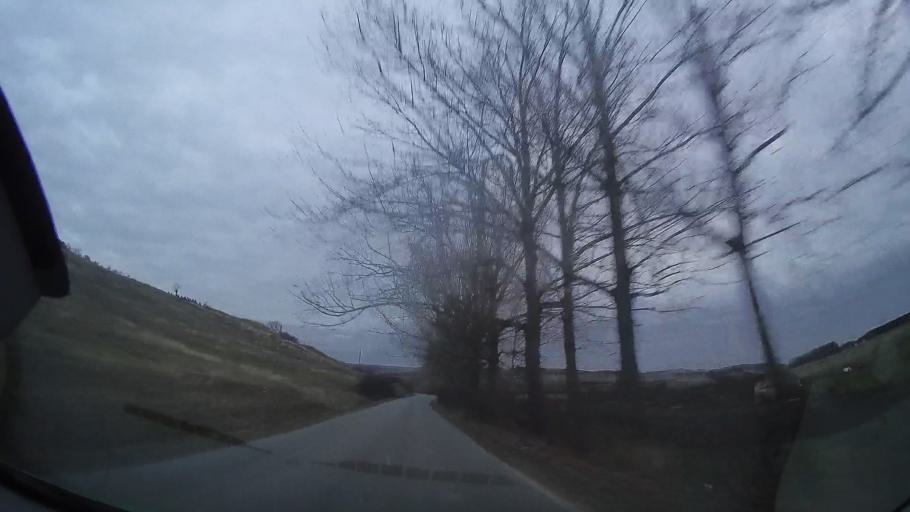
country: RO
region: Cluj
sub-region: Comuna Caianu
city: Caianu
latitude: 46.8062
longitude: 23.9298
